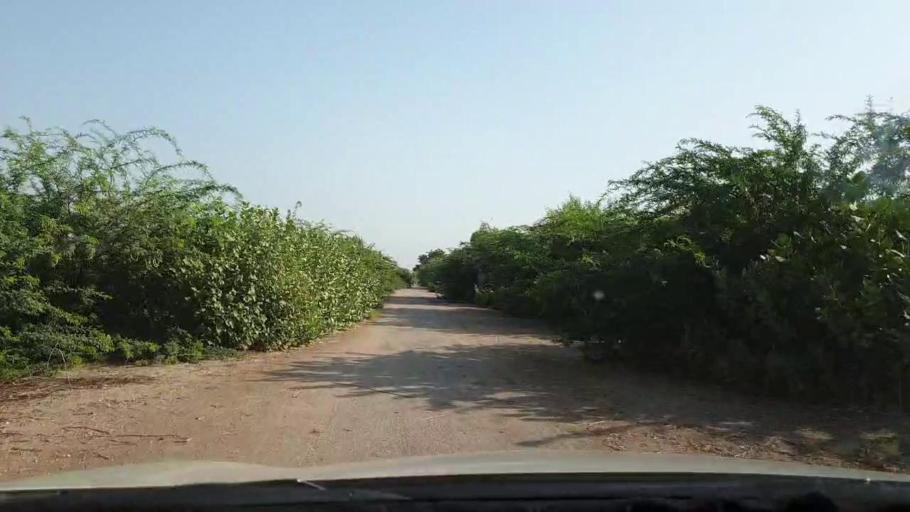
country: PK
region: Sindh
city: Larkana
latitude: 27.5545
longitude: 68.2566
